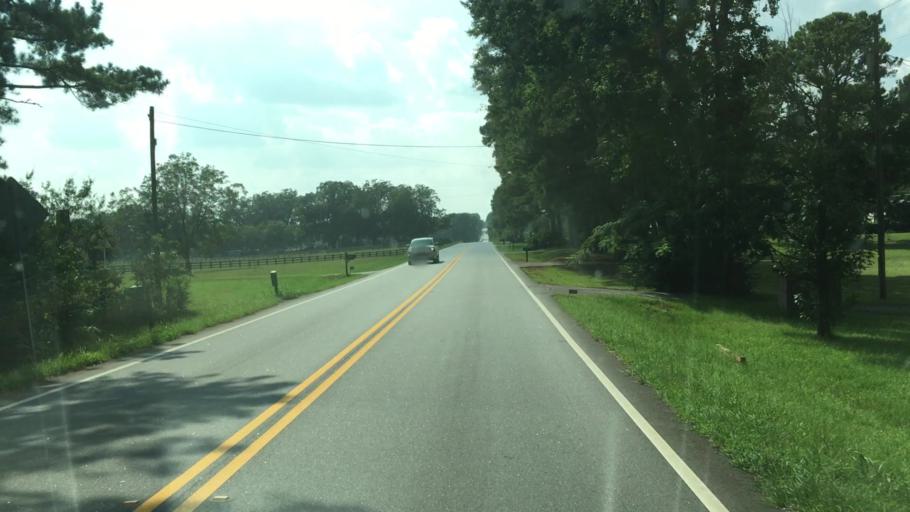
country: US
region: Georgia
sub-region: Jasper County
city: Monticello
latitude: 33.3540
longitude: -83.7284
